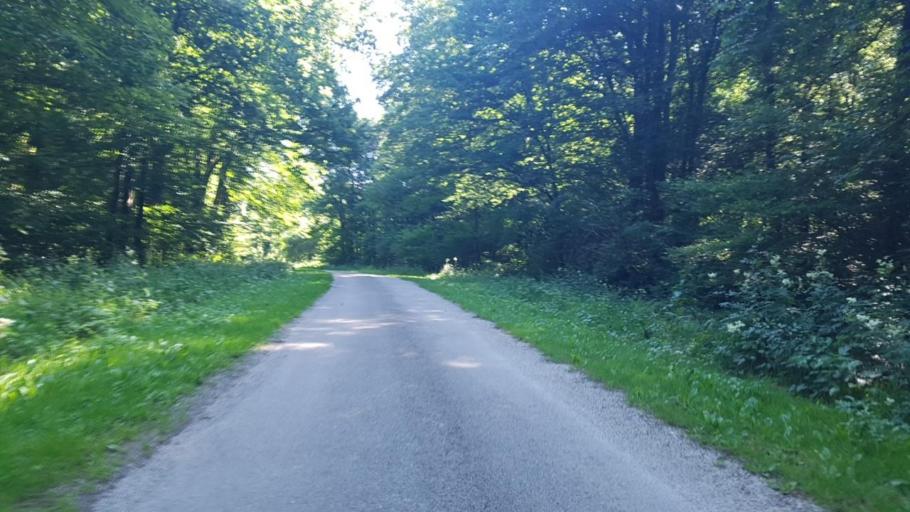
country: FR
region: Picardie
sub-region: Departement de l'Aisne
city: Hirson
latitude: 49.9354
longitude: 4.0897
